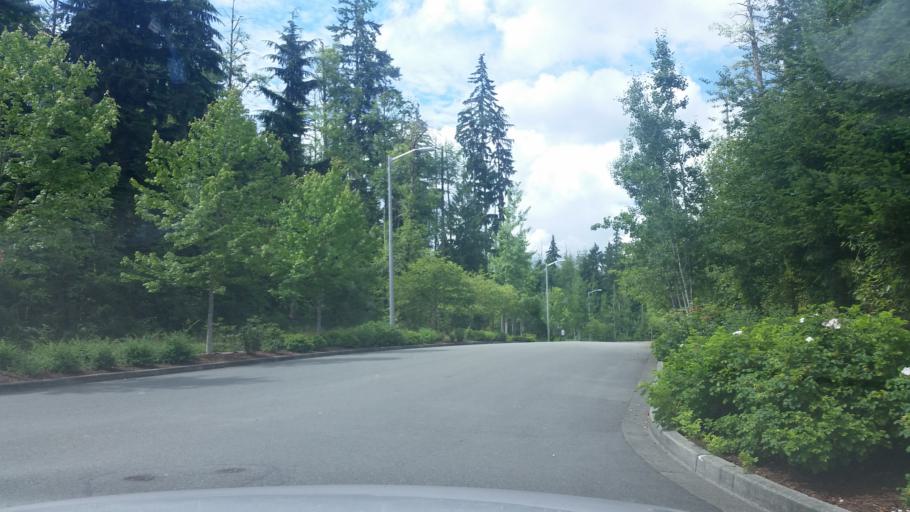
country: US
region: Washington
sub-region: King County
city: Union Hill-Novelty Hill
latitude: 47.6903
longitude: -122.0321
